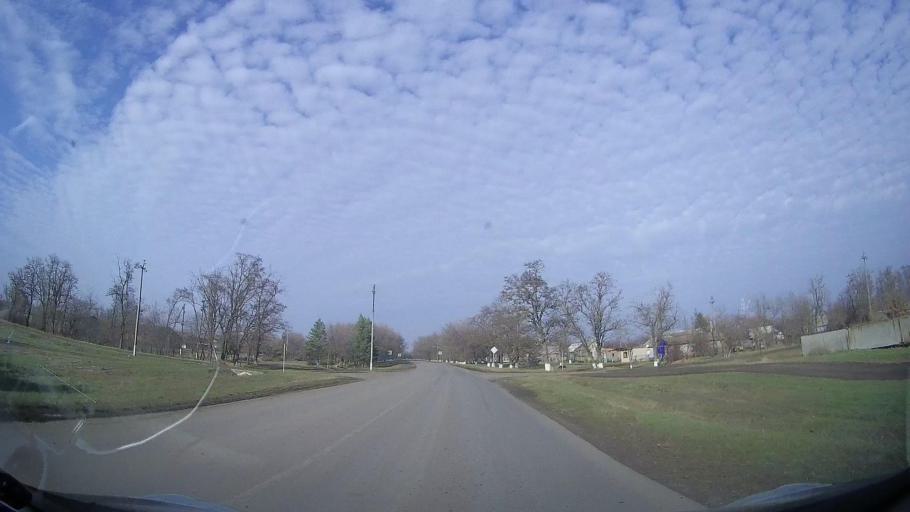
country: RU
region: Rostov
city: Gigant
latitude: 46.8350
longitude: 41.3341
